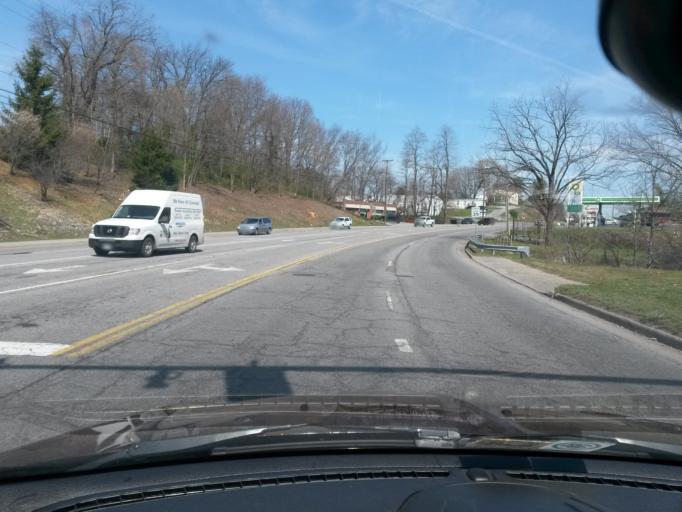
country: US
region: Virginia
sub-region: Montgomery County
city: Christiansburg
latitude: 37.1326
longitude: -80.4126
